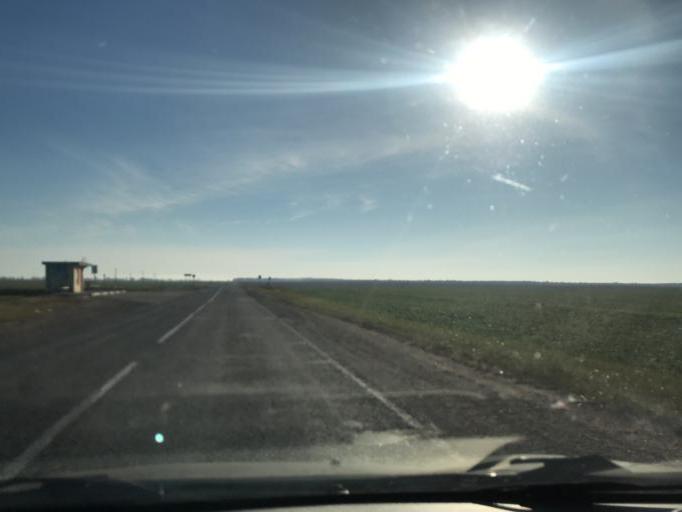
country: BY
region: Gomel
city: Brahin
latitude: 51.7925
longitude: 30.1684
